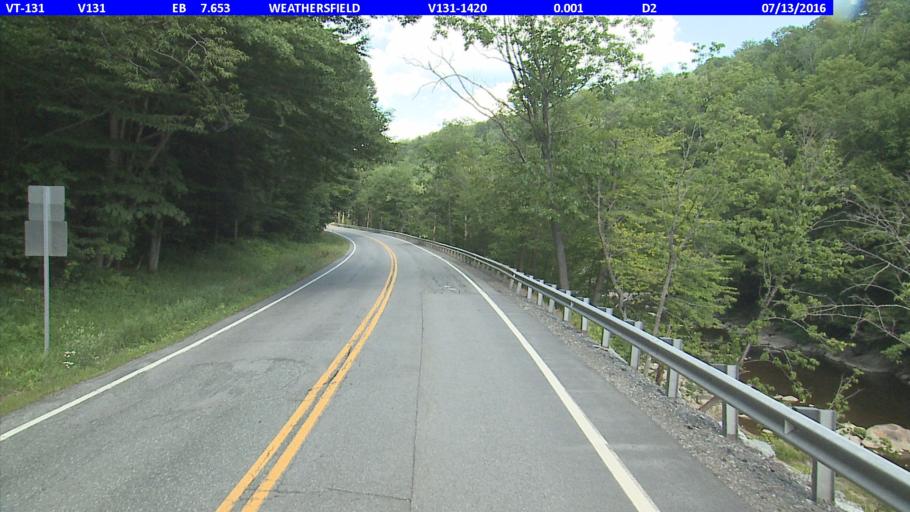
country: US
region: Vermont
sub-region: Windsor County
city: Springfield
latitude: 43.3935
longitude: -72.5379
